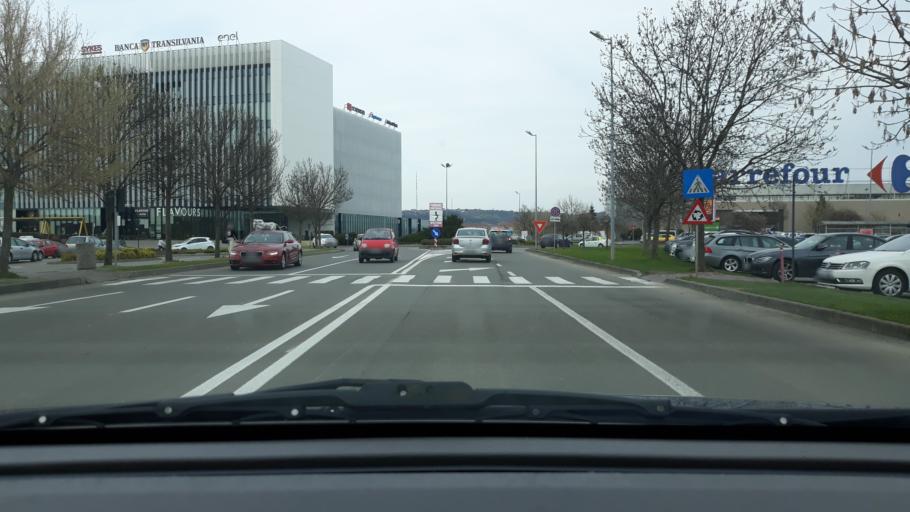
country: RO
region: Bihor
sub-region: Comuna Biharea
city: Oradea
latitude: 47.0359
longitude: 21.9476
